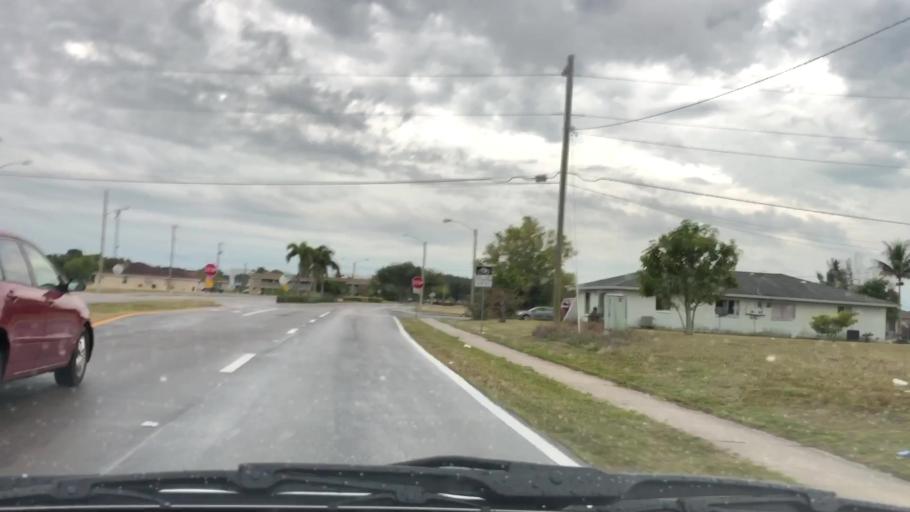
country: US
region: Florida
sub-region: Lee County
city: Lochmoor Waterway Estates
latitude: 26.6368
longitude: -81.9588
